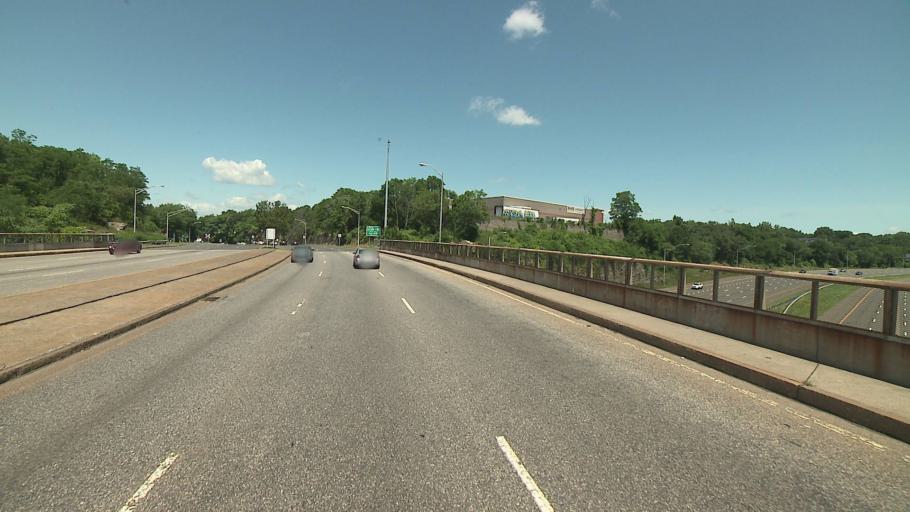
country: US
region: Connecticut
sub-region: Fairfield County
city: Trumbull
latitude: 41.2062
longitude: -73.1907
